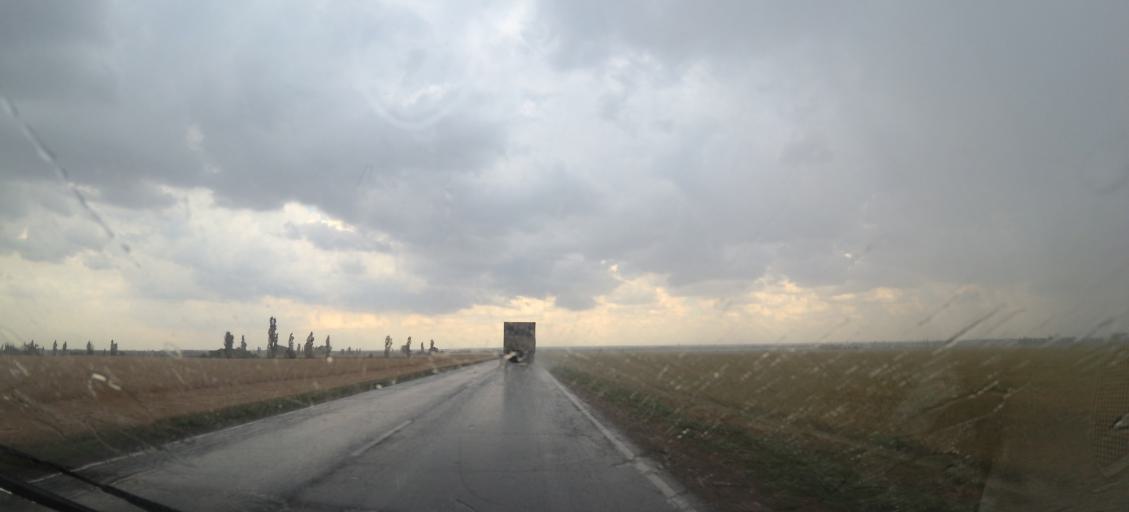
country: RU
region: Rostov
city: Orlovskiy
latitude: 46.8645
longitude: 41.9602
